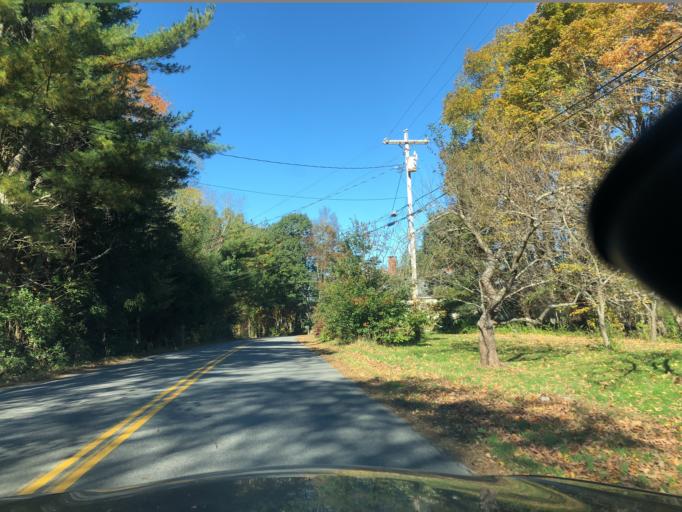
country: US
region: New Hampshire
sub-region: Strafford County
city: Lee
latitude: 43.1207
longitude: -70.9792
